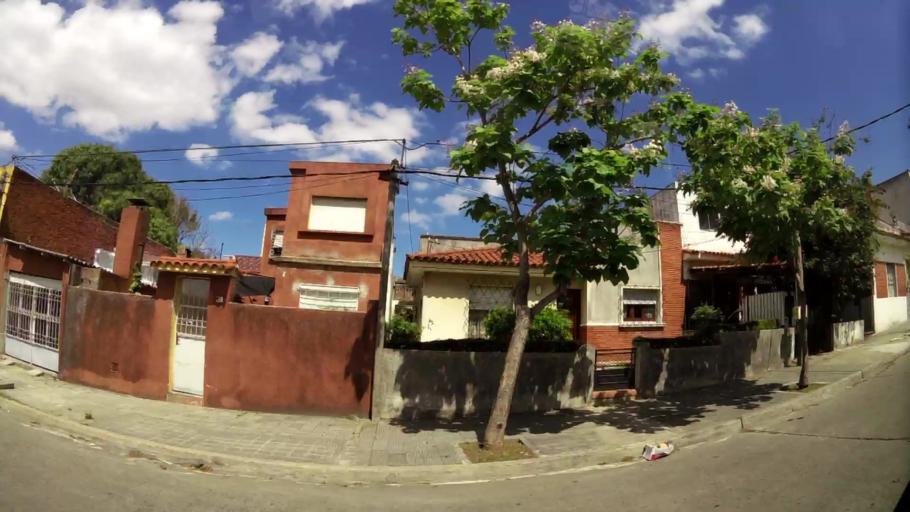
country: UY
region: Montevideo
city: Montevideo
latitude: -34.8597
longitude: -56.2221
